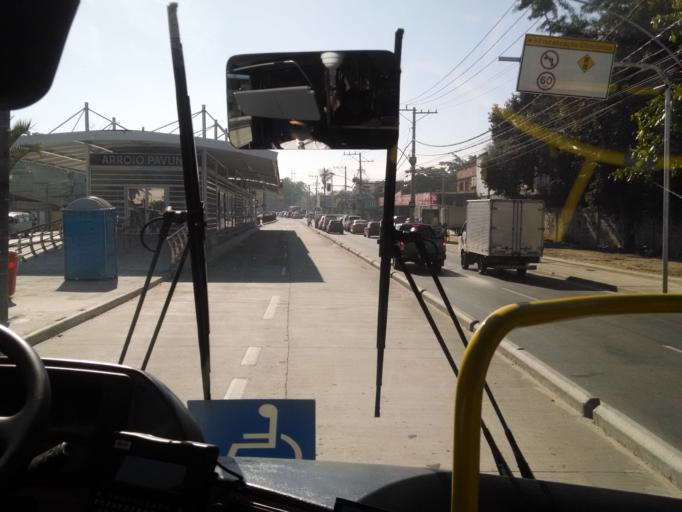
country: BR
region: Rio de Janeiro
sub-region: Sao Joao De Meriti
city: Sao Joao de Meriti
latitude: -22.9556
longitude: -43.3777
